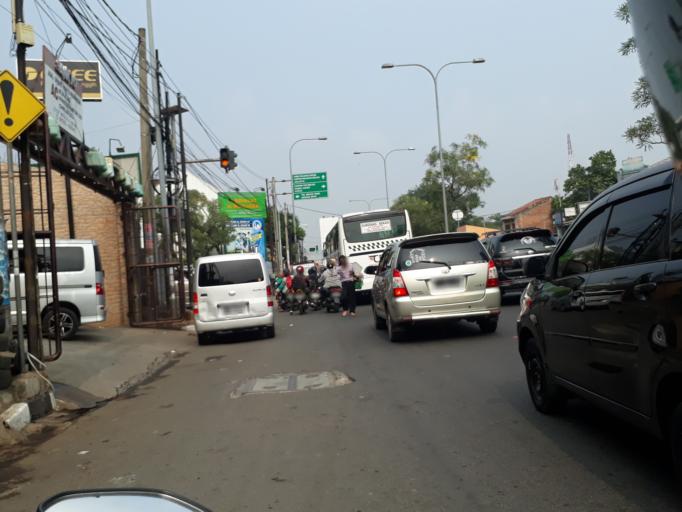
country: ID
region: West Java
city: Bekasi
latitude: -6.2520
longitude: 107.0128
